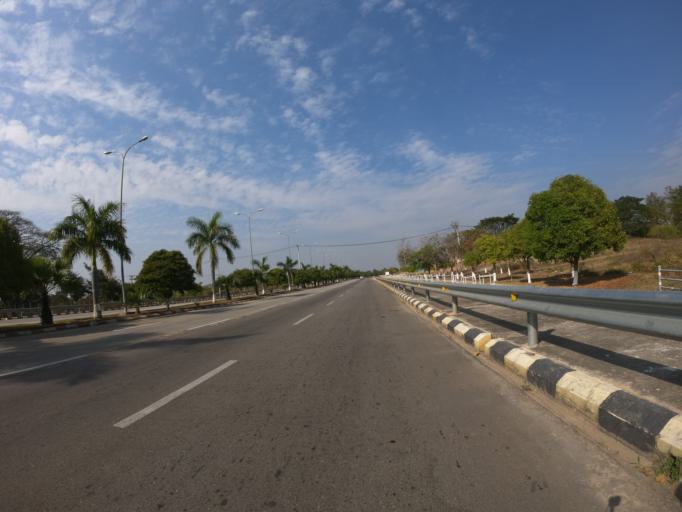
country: MM
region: Mandalay
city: Nay Pyi Taw
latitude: 19.6653
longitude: 96.1206
